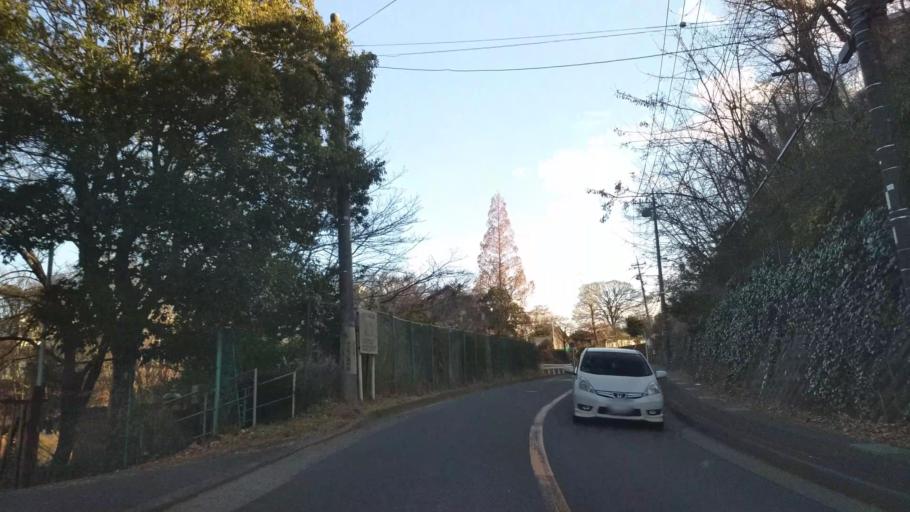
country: JP
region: Kanagawa
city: Ninomiya
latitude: 35.3467
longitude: 139.2693
